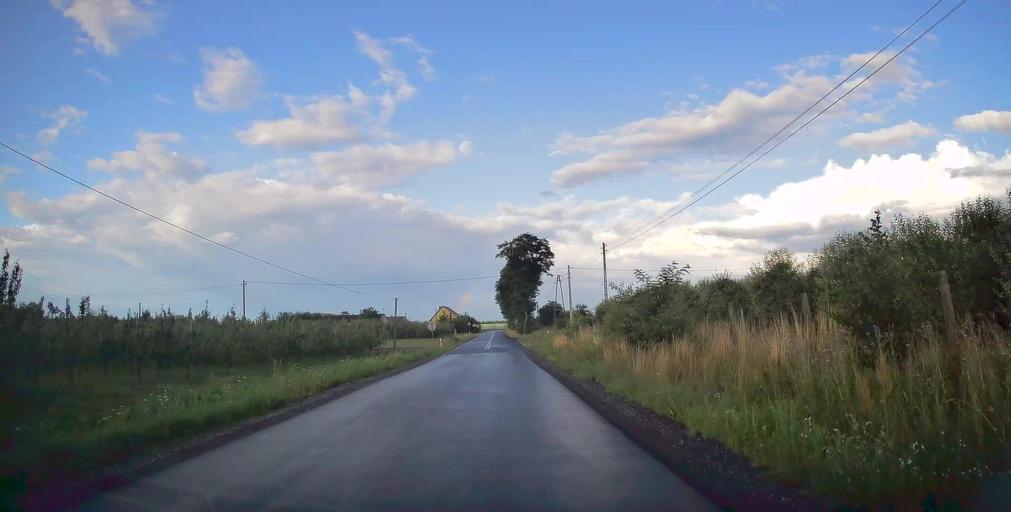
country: PL
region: Masovian Voivodeship
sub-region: Powiat grojecki
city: Goszczyn
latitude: 51.7640
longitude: 20.8977
